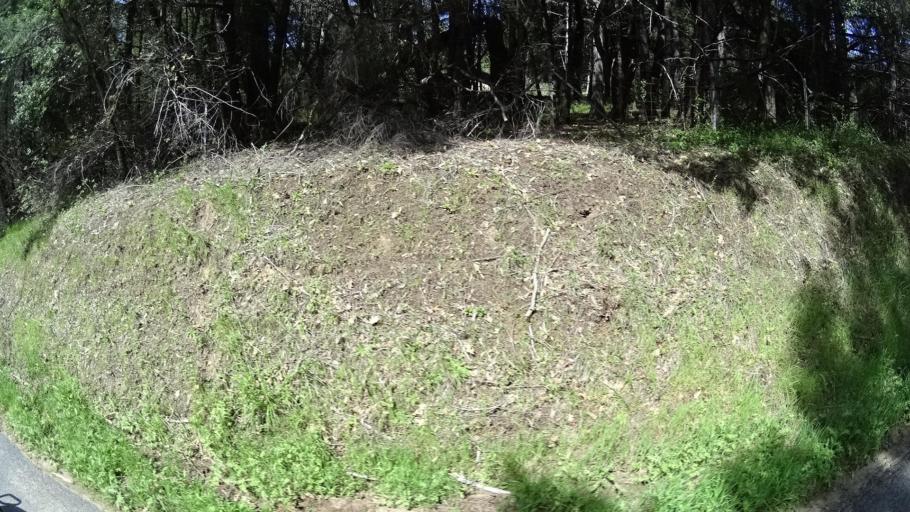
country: US
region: California
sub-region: Humboldt County
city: Redway
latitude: 40.3505
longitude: -123.7165
